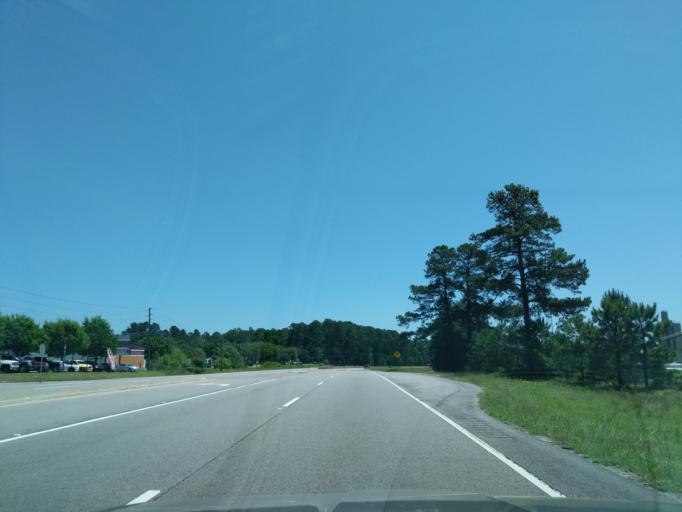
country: US
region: Georgia
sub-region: Columbia County
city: Martinez
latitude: 33.5249
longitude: -82.0432
